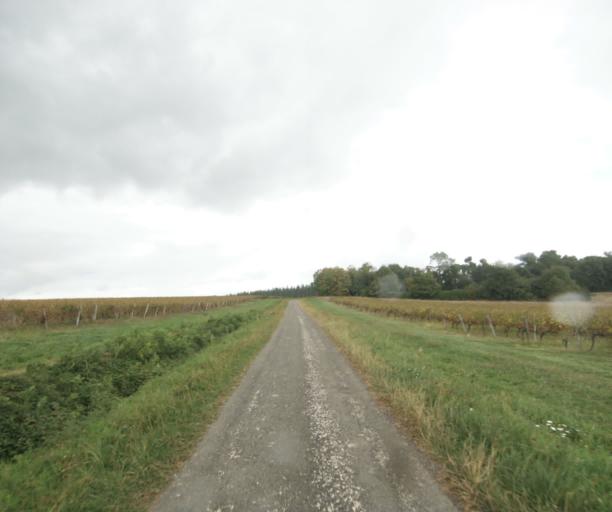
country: FR
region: Midi-Pyrenees
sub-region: Departement du Gers
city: Eauze
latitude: 43.8776
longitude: 0.0714
